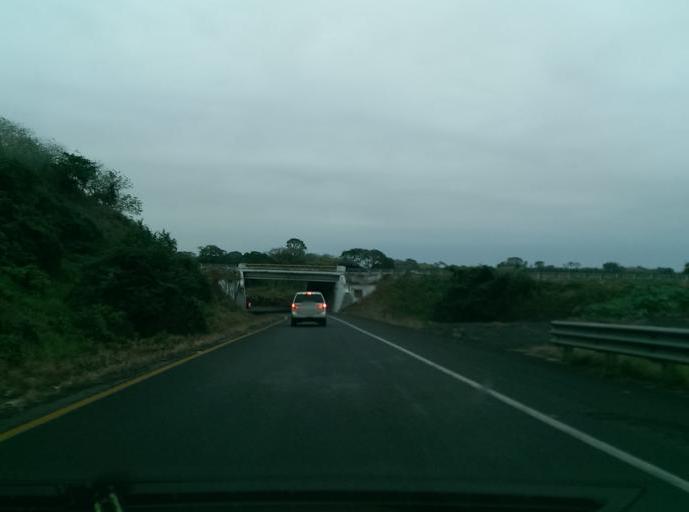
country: MX
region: Veracruz
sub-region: Tierra Blanca
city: Huixcolotla
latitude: 18.7803
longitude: -96.4593
